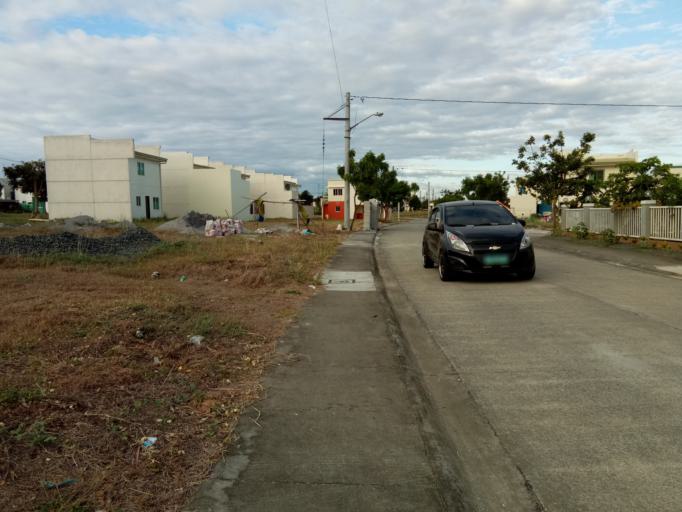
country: PH
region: Calabarzon
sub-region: Province of Cavite
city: Biga
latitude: 14.2766
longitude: 120.9686
